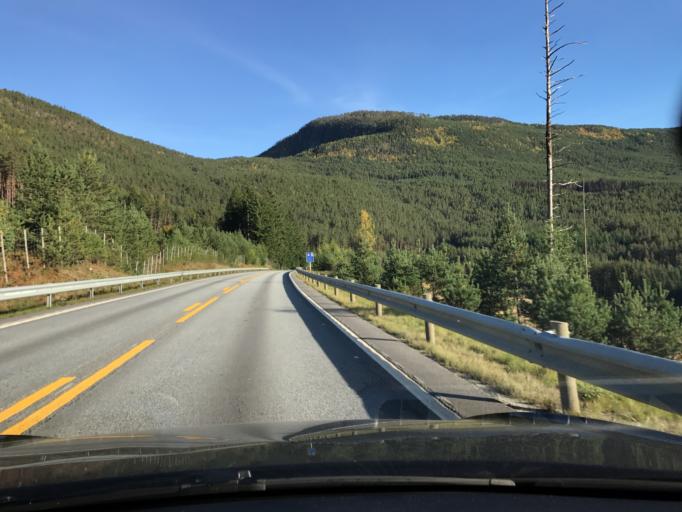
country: NO
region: Sogn og Fjordane
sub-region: Sogndal
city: Sogndalsfjora
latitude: 61.1815
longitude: 7.2898
